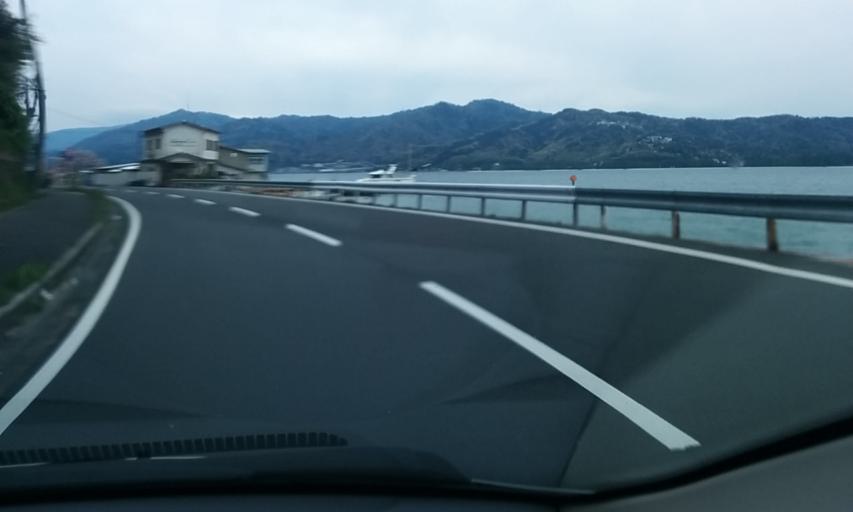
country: JP
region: Kyoto
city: Miyazu
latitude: 35.5609
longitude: 135.2057
